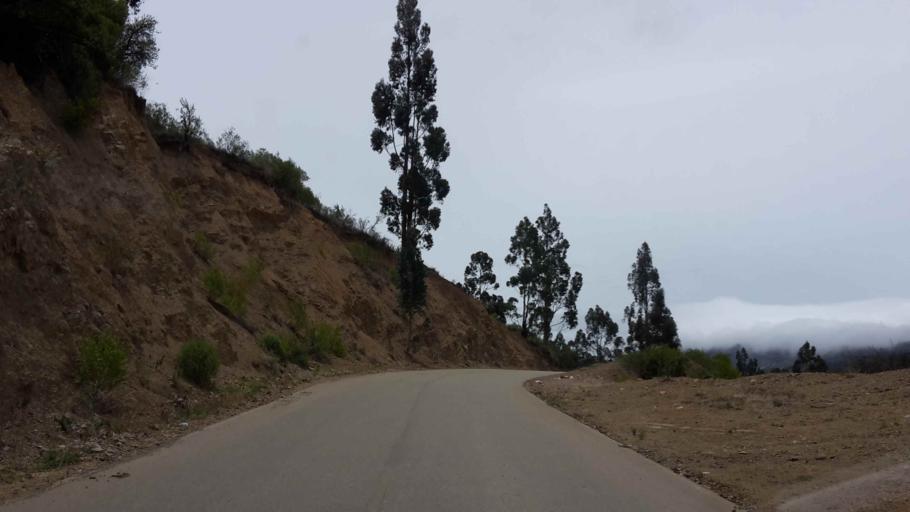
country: BO
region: Cochabamba
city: Totora
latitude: -17.7022
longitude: -65.2140
